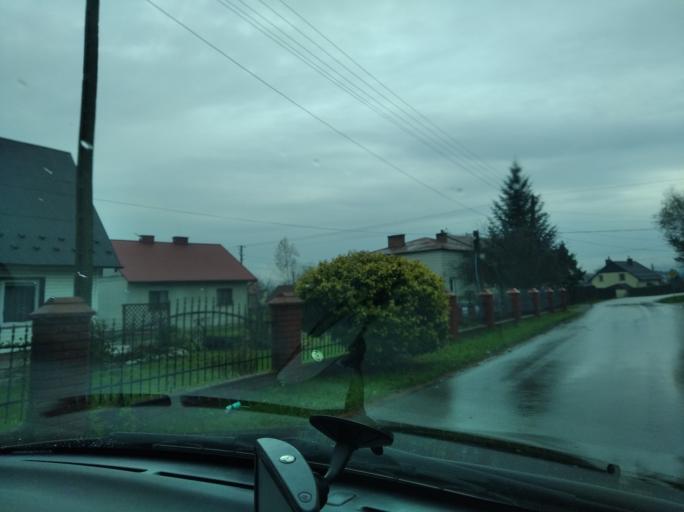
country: PL
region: Subcarpathian Voivodeship
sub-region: Powiat strzyzowski
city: Czudec
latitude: 49.9425
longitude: 21.8413
